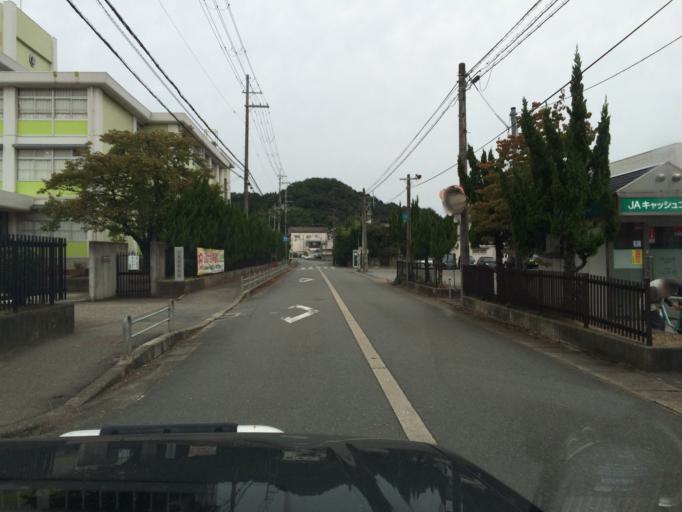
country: JP
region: Hyogo
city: Toyooka
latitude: 35.4684
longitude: 134.7741
